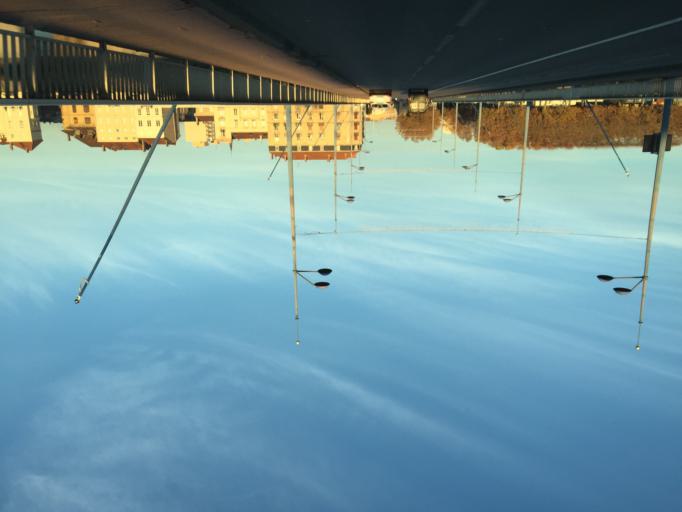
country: FR
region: Rhone-Alpes
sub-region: Departement de la Loire
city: Le Coteau
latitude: 46.0319
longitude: 4.0820
